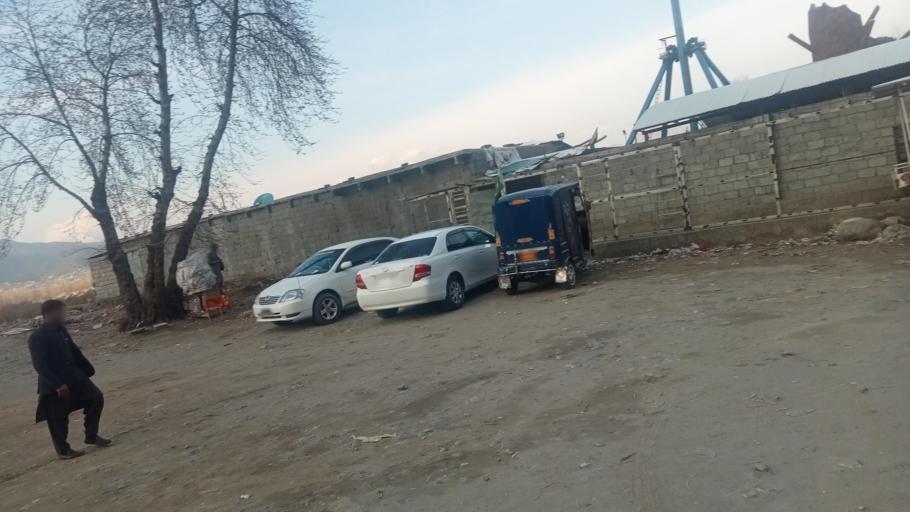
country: PK
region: Khyber Pakhtunkhwa
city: Mingora
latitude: 34.7918
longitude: 72.3914
